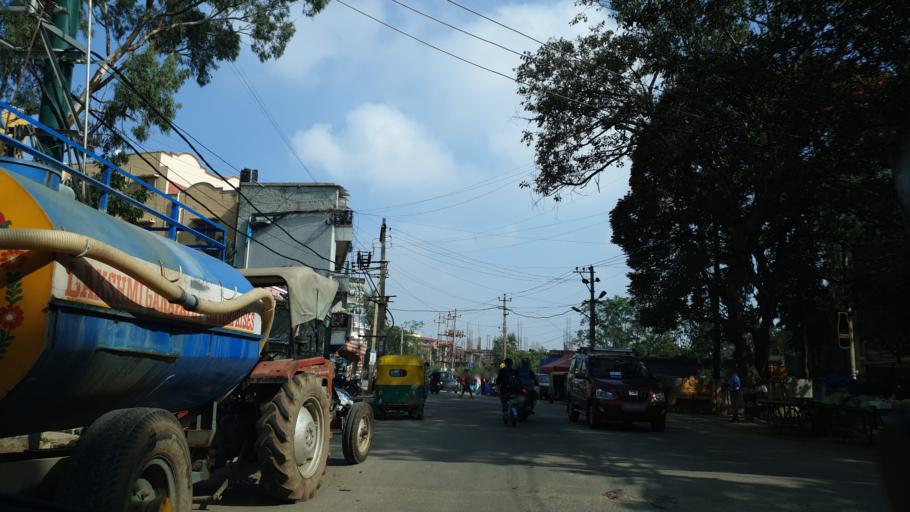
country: IN
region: Karnataka
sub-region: Bangalore Urban
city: Bangalore
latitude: 12.9693
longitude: 77.6825
